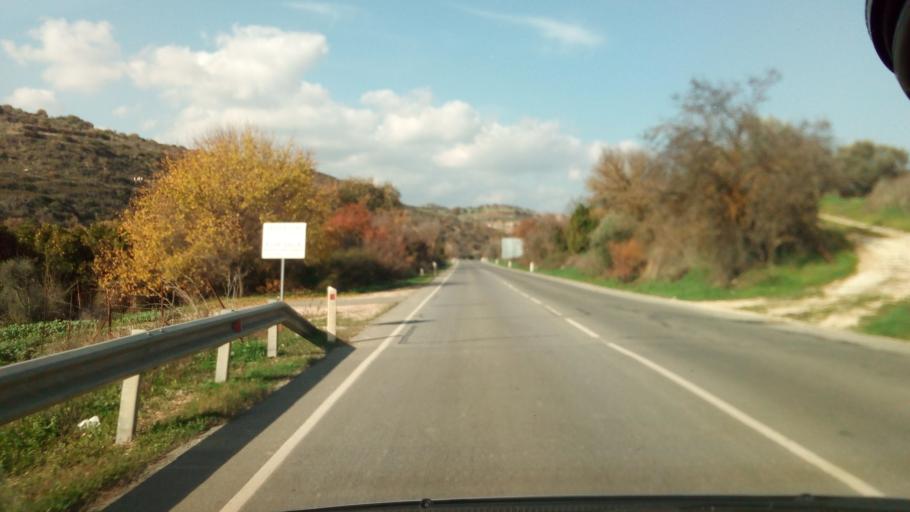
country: CY
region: Pafos
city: Polis
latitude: 34.9558
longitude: 32.4658
